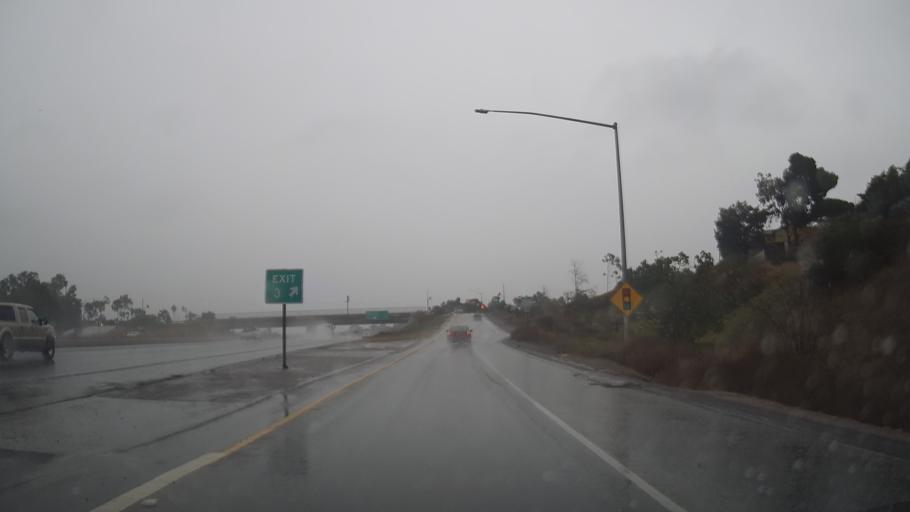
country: US
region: California
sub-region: San Diego County
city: Bonita
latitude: 32.6634
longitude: -117.0604
